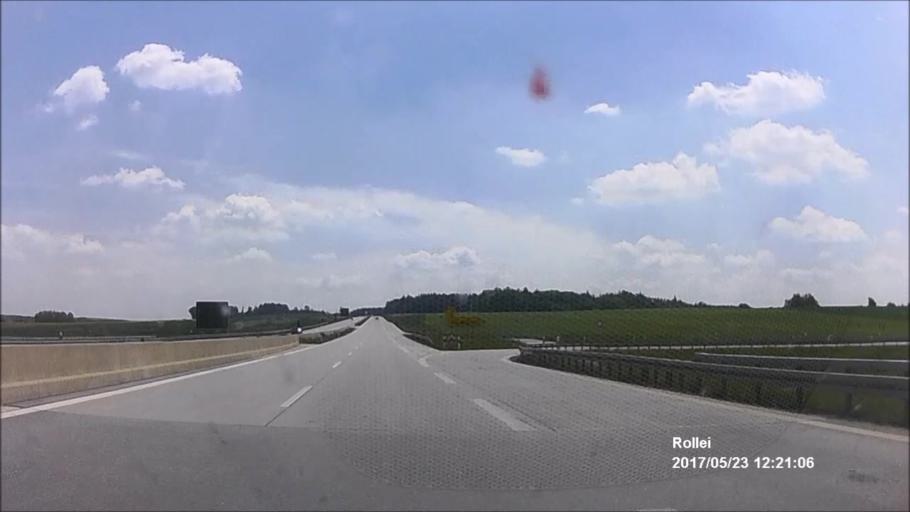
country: DE
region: Bavaria
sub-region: Lower Bavaria
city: Ergoldsbach
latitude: 48.7303
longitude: 12.1607
